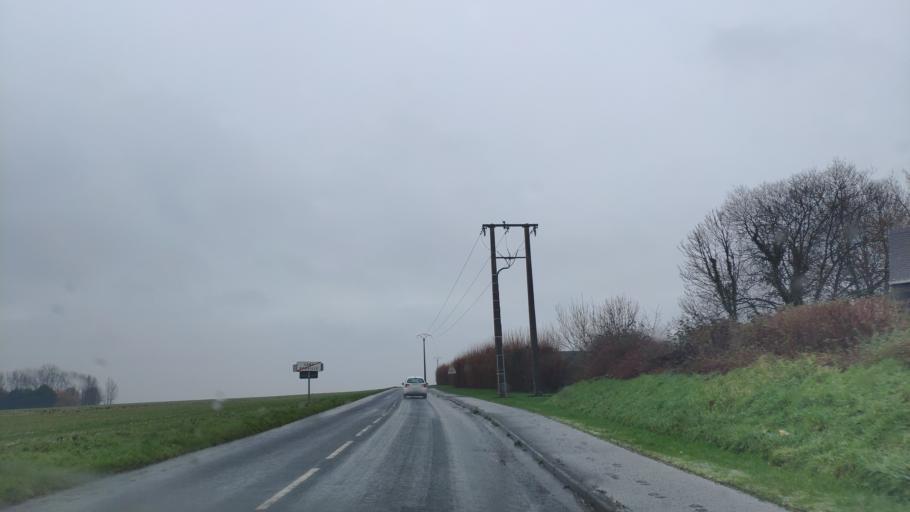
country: FR
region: Haute-Normandie
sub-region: Departement de la Seine-Maritime
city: Cany-Barville
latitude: 49.7892
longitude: 0.6483
